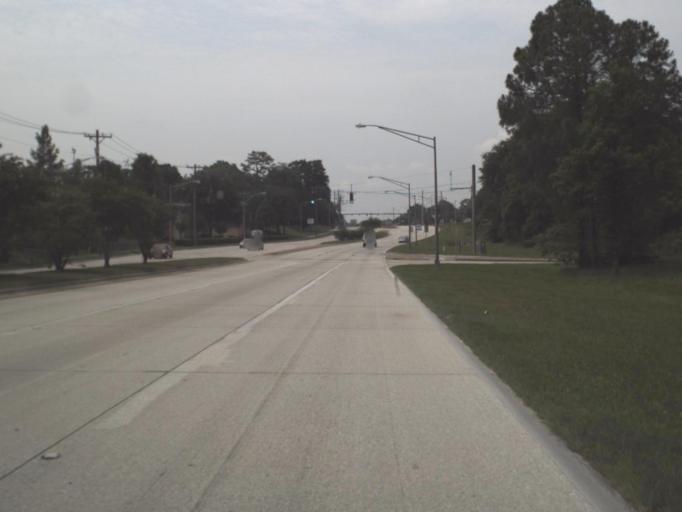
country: US
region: Florida
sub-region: Duval County
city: Jacksonville
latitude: 30.2929
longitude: -81.7202
